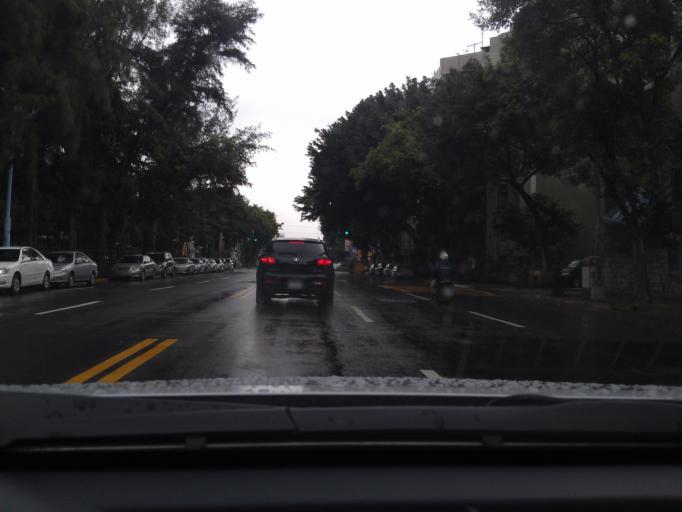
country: TW
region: Taipei
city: Taipei
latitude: 25.0986
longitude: 121.5354
